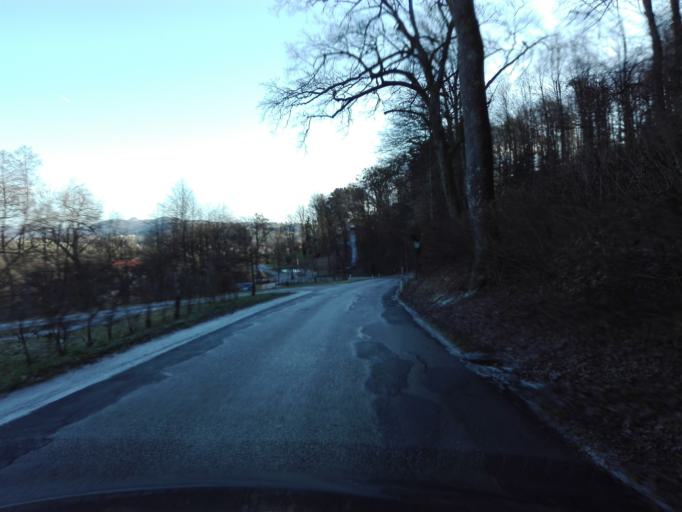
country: AT
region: Upper Austria
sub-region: Politischer Bezirk Perg
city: Bad Kreuzen
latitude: 48.2223
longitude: 14.7736
